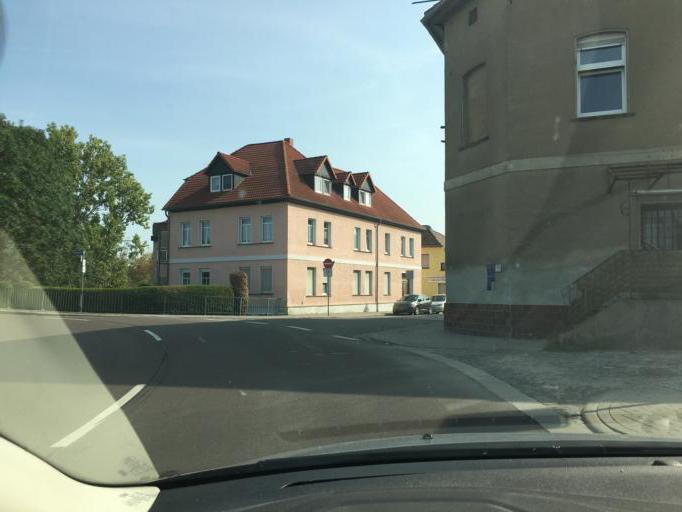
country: DE
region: Saxony-Anhalt
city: Nienburg/Saale
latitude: 51.8392
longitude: 11.7711
